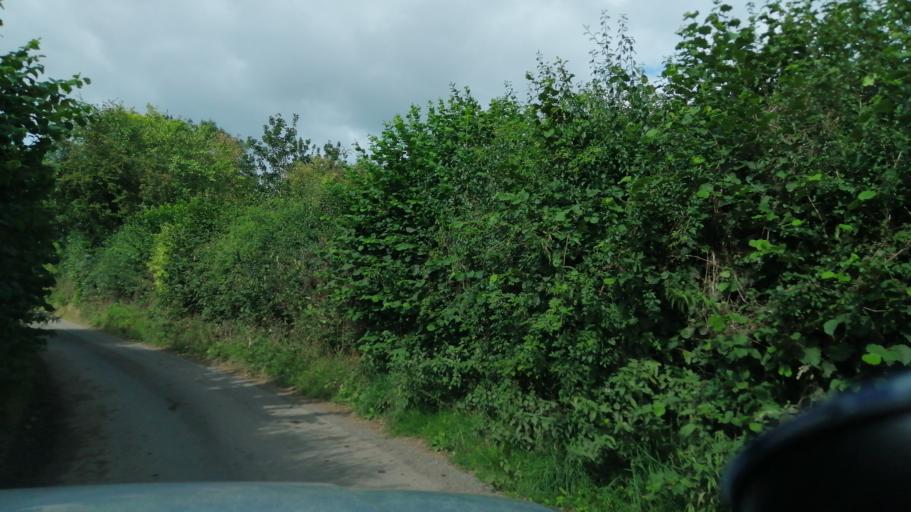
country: GB
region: England
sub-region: Herefordshire
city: Kinnersley
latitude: 52.1357
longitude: -2.9509
